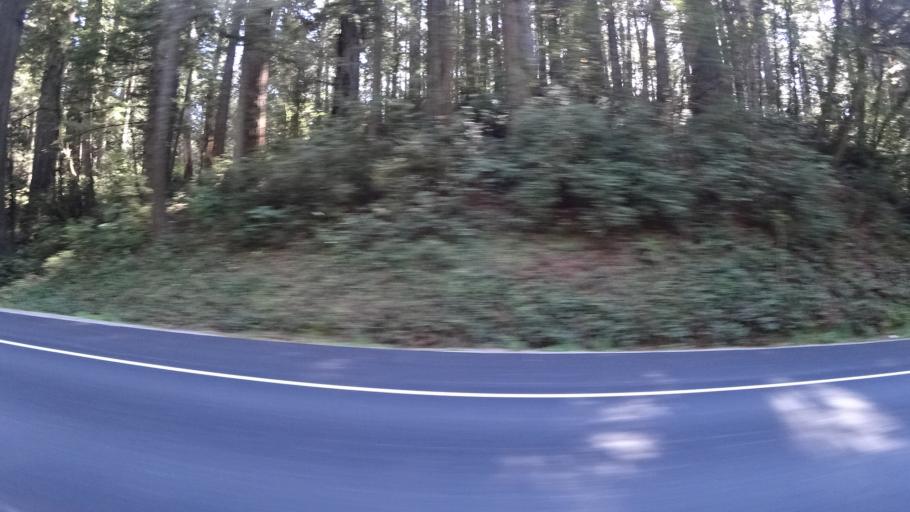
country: US
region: California
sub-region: Del Norte County
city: Bertsch-Oceanview
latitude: 41.6684
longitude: -124.1132
